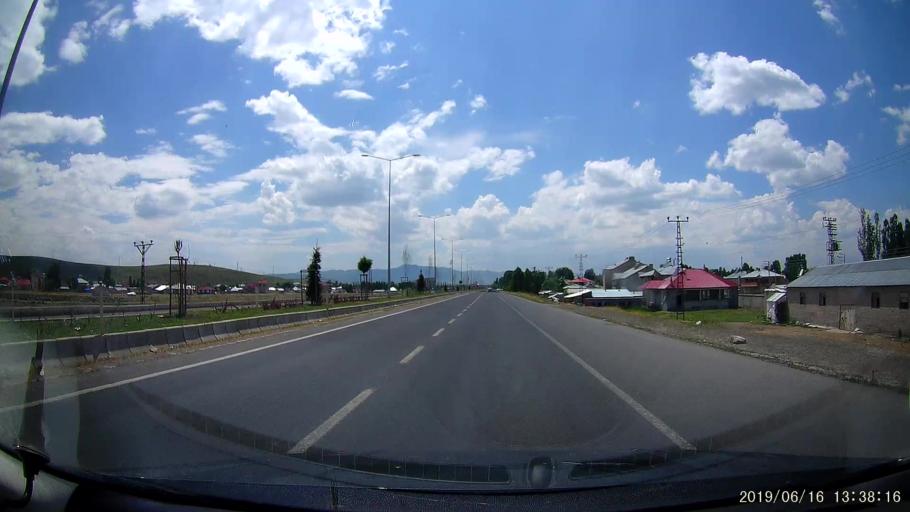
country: TR
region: Agri
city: Agri
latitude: 39.7116
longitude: 43.0764
